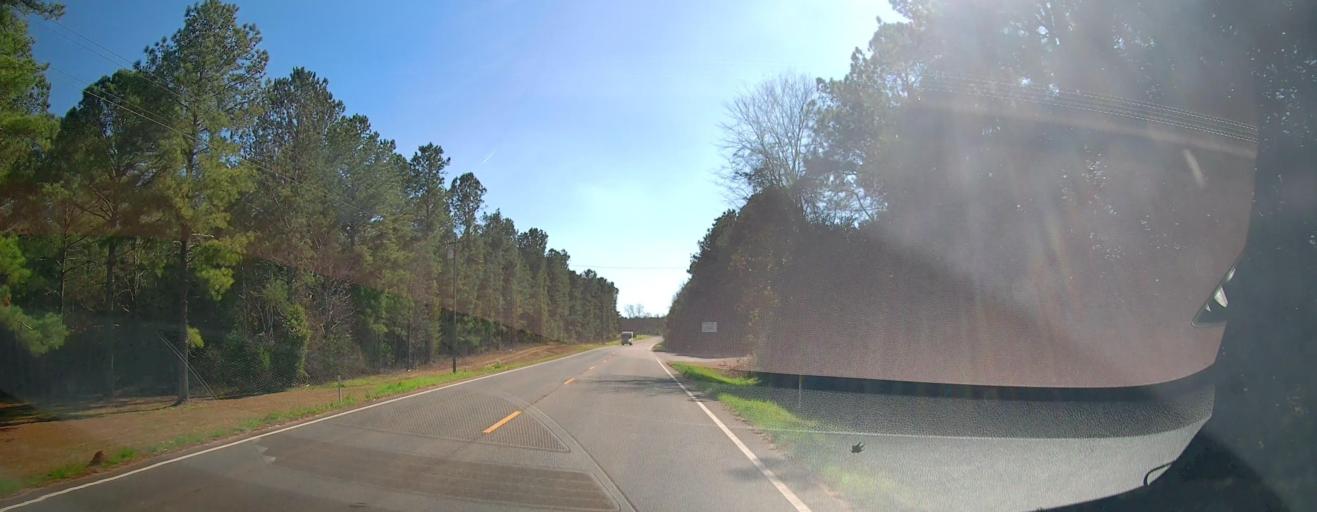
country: US
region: Georgia
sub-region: Macon County
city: Montezuma
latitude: 32.3637
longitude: -84.0138
